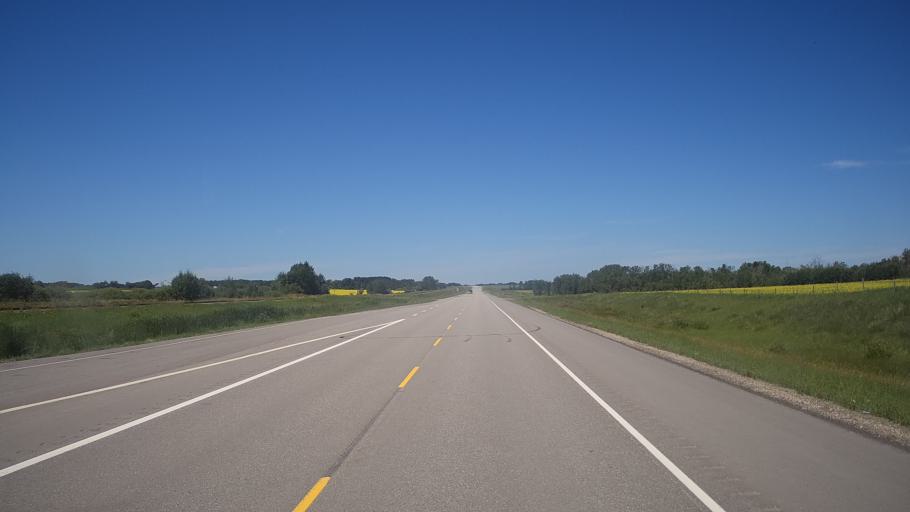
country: CA
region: Manitoba
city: Minnedosa
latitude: 50.2806
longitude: -99.9571
